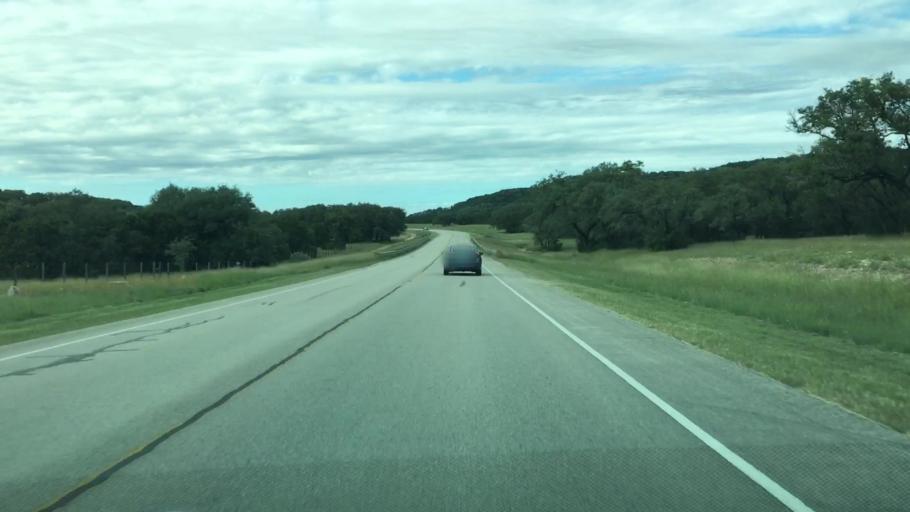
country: US
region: Texas
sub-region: Hays County
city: Wimberley
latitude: 30.0125
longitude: -98.0847
